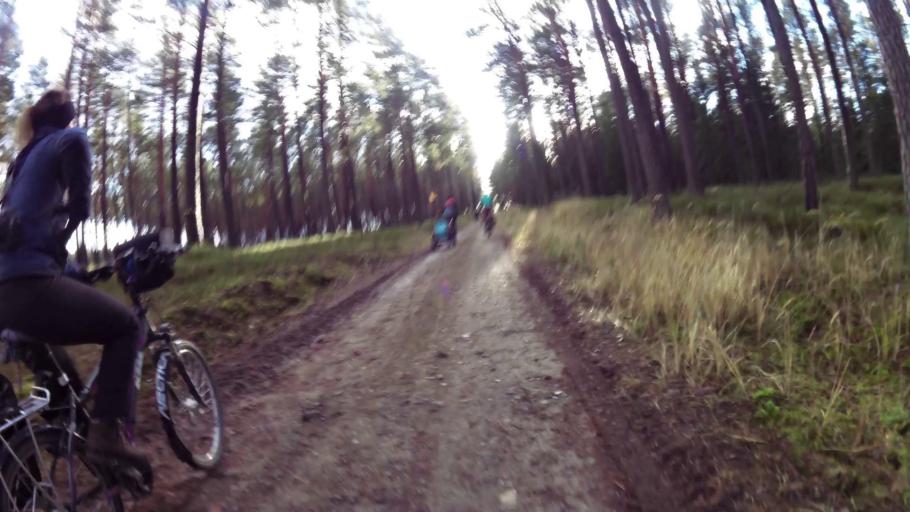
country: PL
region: West Pomeranian Voivodeship
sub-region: Powiat koszalinski
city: Sianow
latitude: 54.0908
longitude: 16.2936
